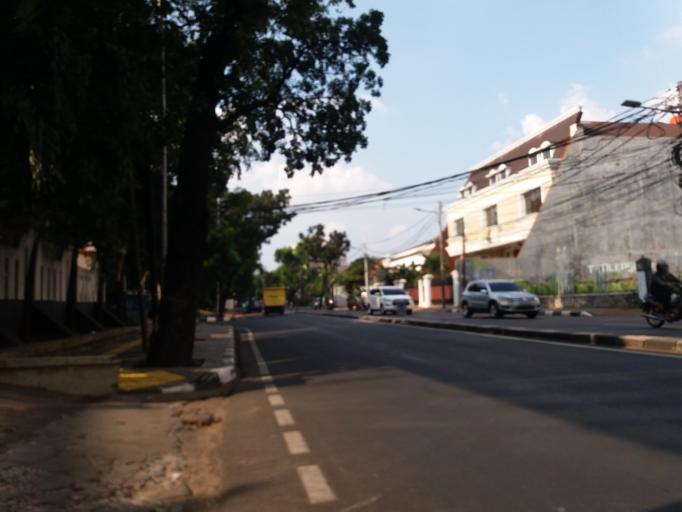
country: ID
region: Jakarta Raya
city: Jakarta
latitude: -6.2472
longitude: 106.8065
